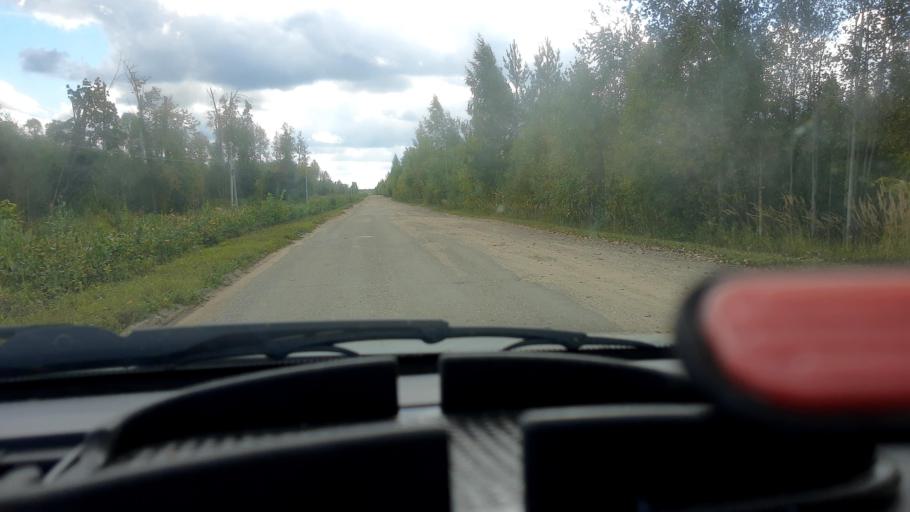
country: RU
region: Mariy-El
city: Kilemary
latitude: 56.8966
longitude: 46.7482
